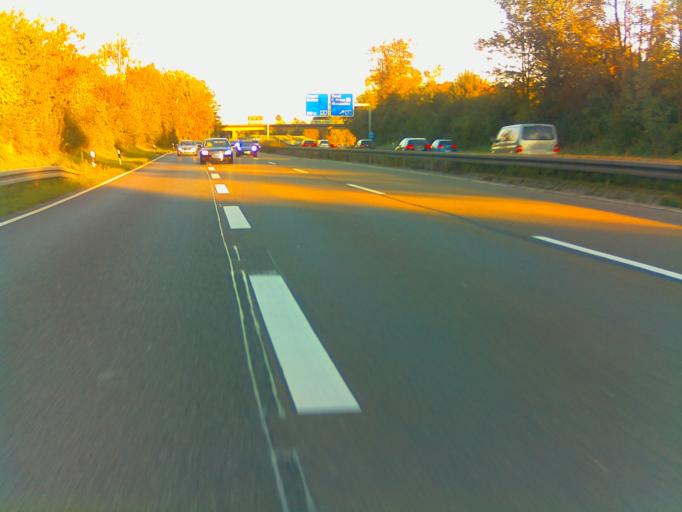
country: DE
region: Hesse
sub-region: Regierungsbezirk Darmstadt
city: Bad Homburg vor der Hoehe
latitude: 50.2032
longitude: 8.6370
